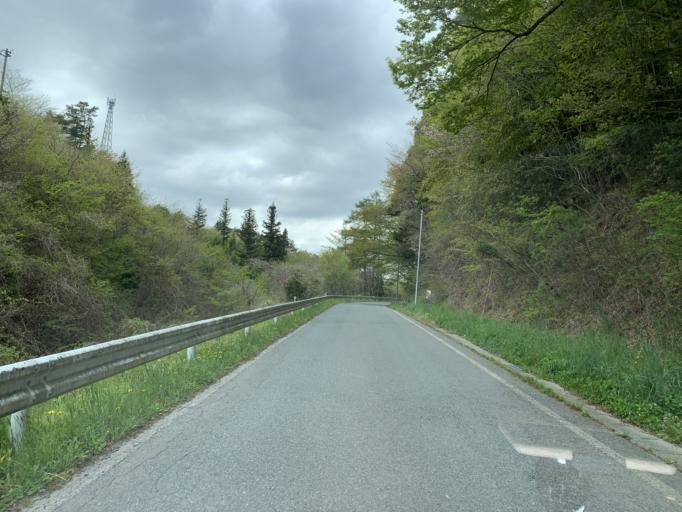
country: JP
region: Iwate
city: Ichinoseki
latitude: 38.7924
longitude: 141.4194
